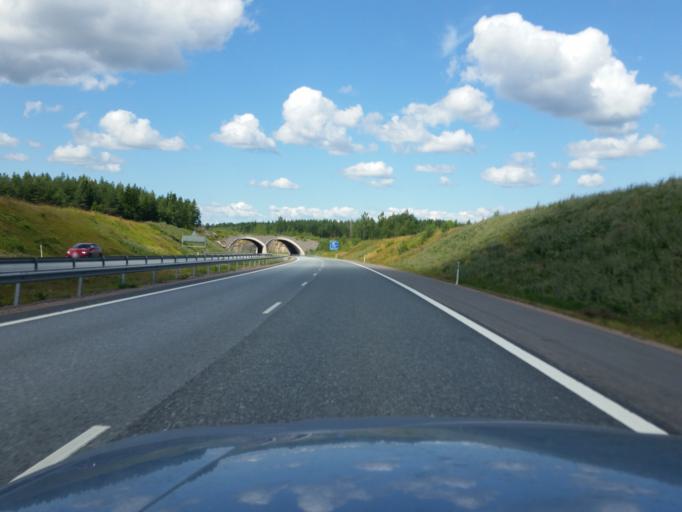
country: FI
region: Uusimaa
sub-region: Helsinki
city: Sammatti
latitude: 60.3756
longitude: 23.8256
